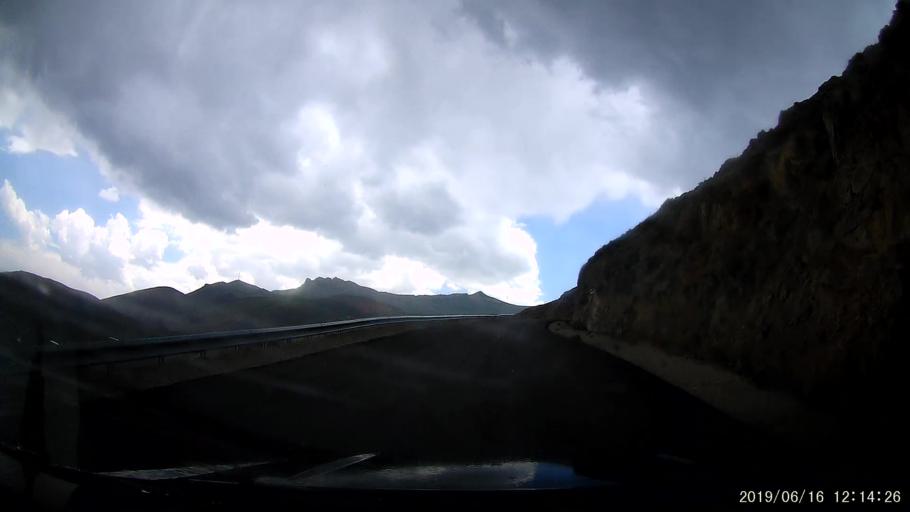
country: TR
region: Agri
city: Dogubayazit
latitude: 39.4462
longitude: 44.2362
